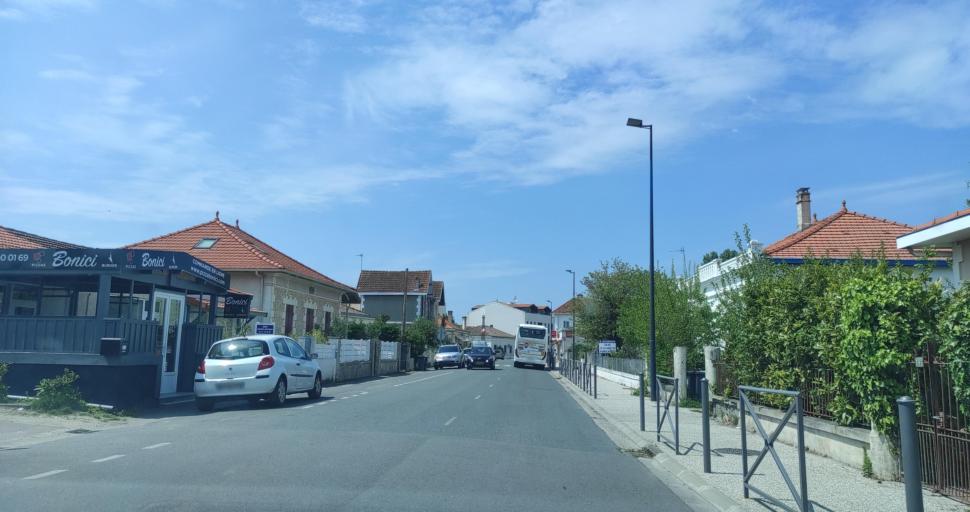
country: FR
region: Aquitaine
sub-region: Departement de la Gironde
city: Ares
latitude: 44.7652
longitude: -1.1366
